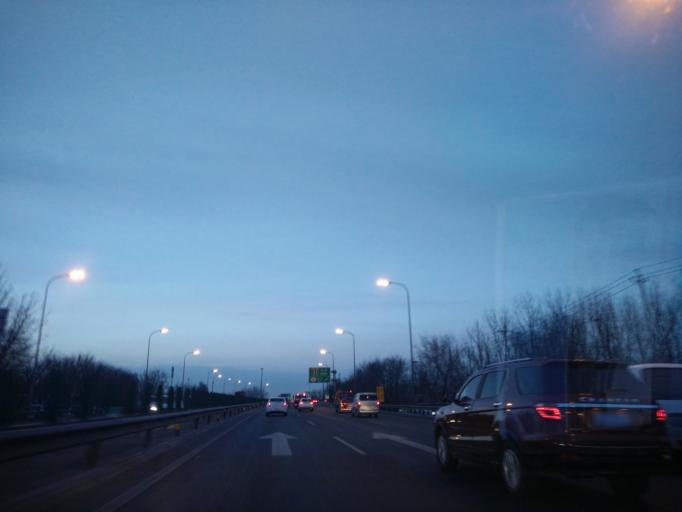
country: CN
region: Beijing
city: Dongfeng
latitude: 39.8747
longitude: 116.5429
